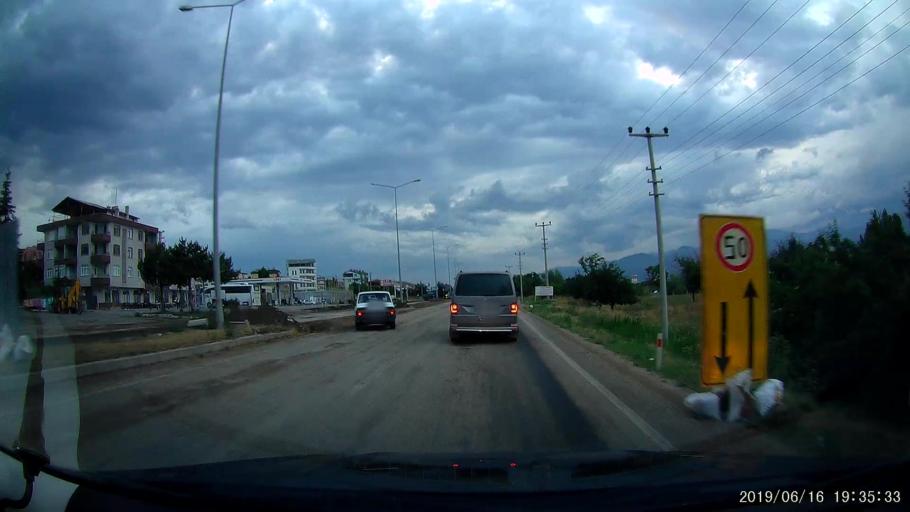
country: TR
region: Sivas
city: Susehri
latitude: 40.1707
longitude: 38.0920
